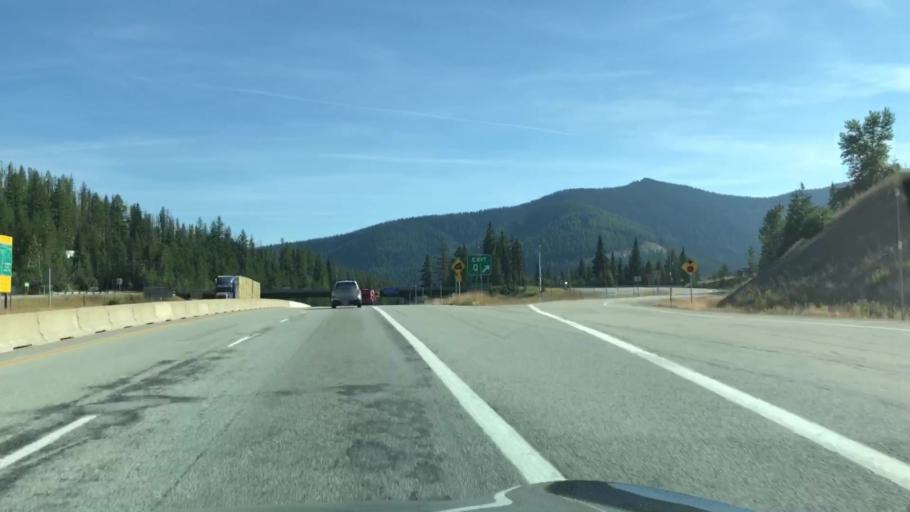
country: US
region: Idaho
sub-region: Shoshone County
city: Wallace
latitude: 47.4553
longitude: -115.6952
